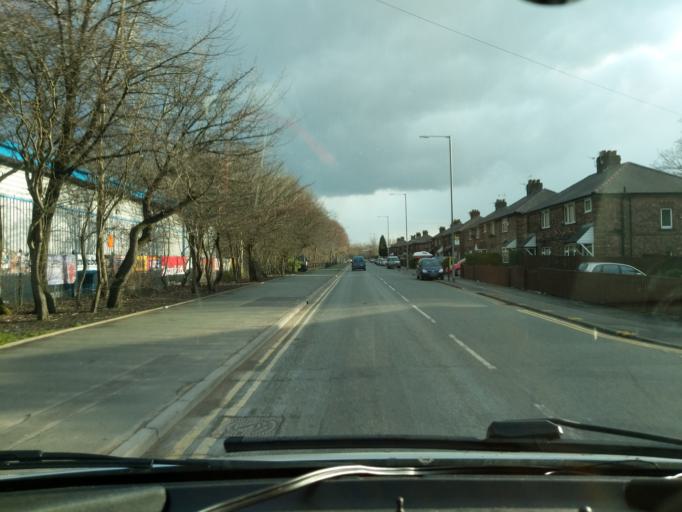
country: GB
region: England
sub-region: St. Helens
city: St Helens
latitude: 53.4464
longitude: -2.7197
